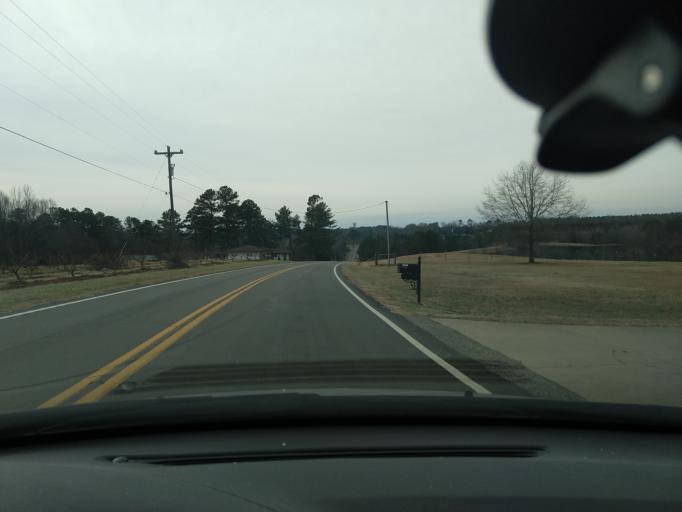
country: US
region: South Carolina
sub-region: Spartanburg County
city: Cowpens
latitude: 35.0490
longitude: -81.7900
